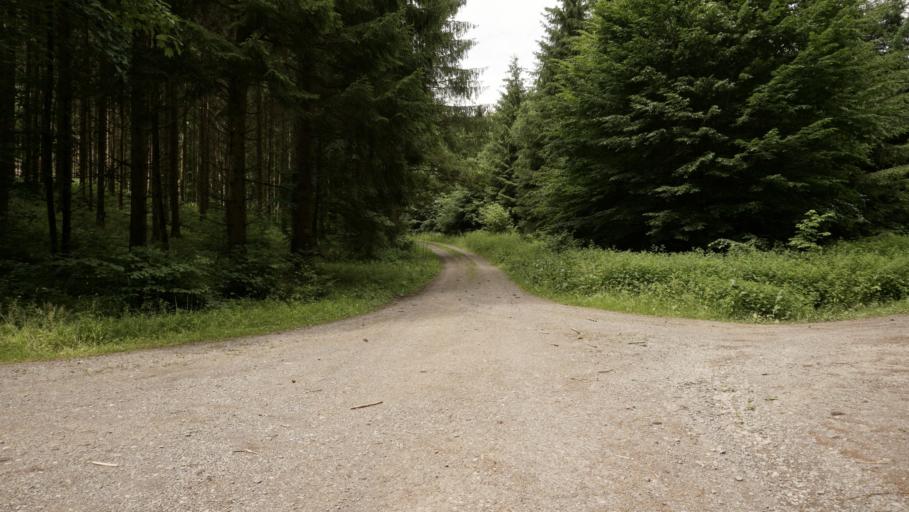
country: DE
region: Baden-Wuerttemberg
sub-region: Karlsruhe Region
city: Mosbach
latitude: 49.3263
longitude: 9.1985
